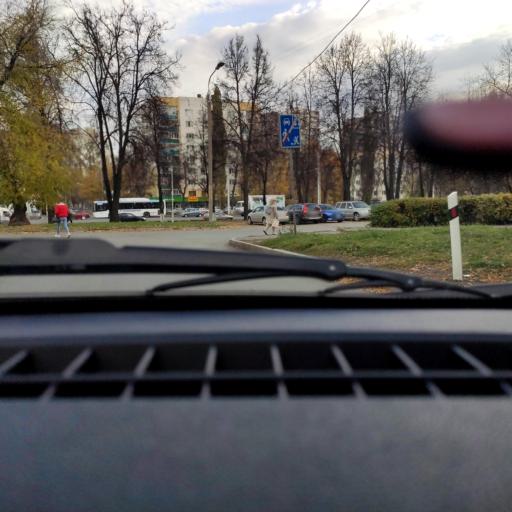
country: RU
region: Bashkortostan
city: Ufa
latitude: 54.7595
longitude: 56.0082
